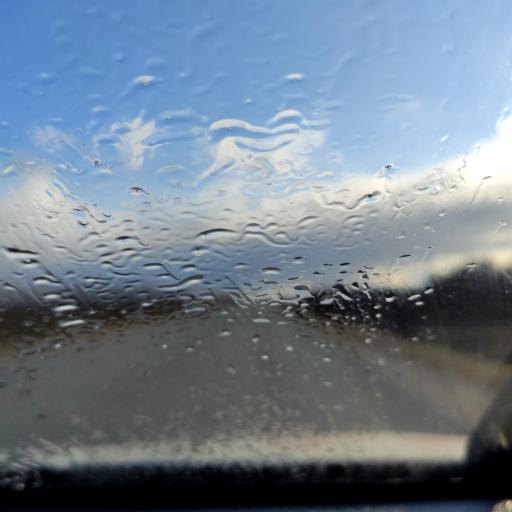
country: RU
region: Bashkortostan
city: Avdon
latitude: 54.5695
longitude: 55.6919
